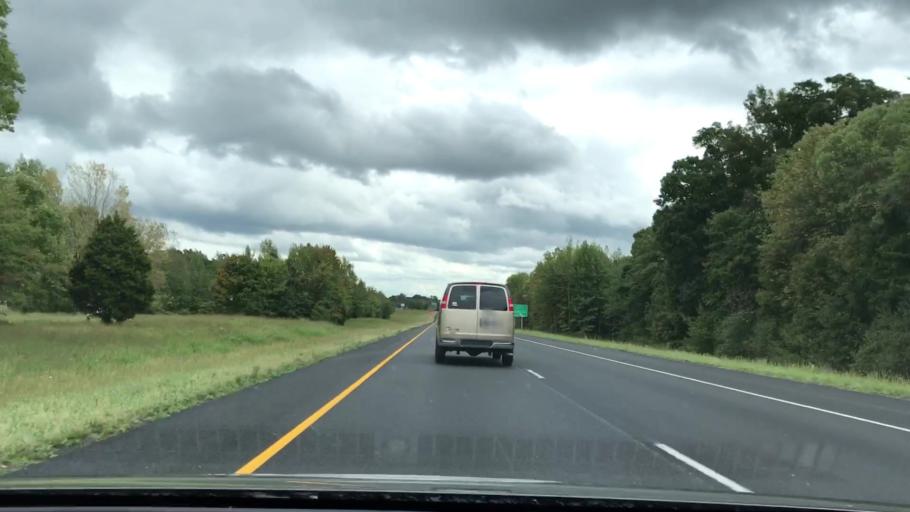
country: US
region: Tennessee
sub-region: Cheatham County
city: Pleasant View
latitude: 36.3941
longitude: -87.0111
